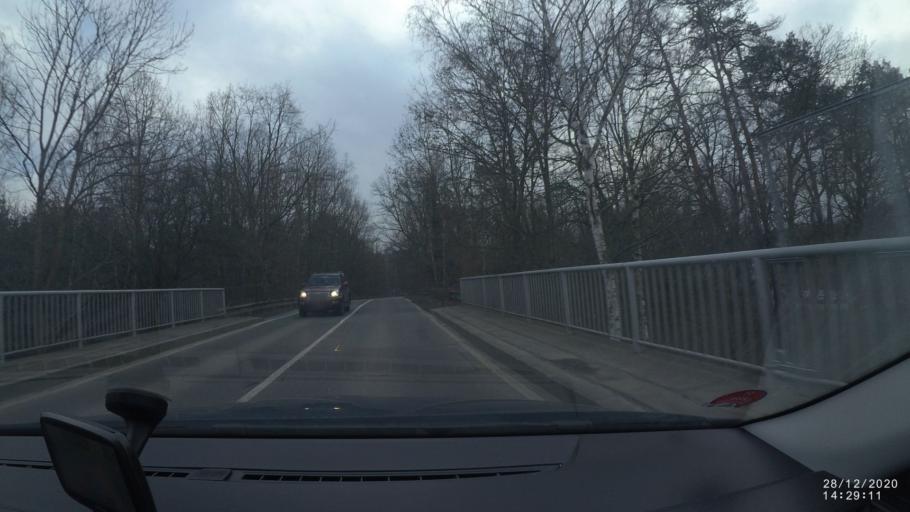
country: CZ
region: Central Bohemia
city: Sestajovice
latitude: 50.0875
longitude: 14.6662
